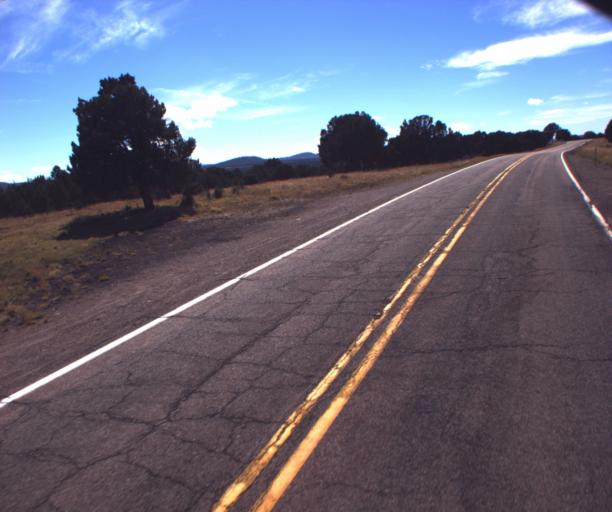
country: US
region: Arizona
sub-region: Navajo County
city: White Mountain Lake
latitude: 34.2914
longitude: -109.8076
